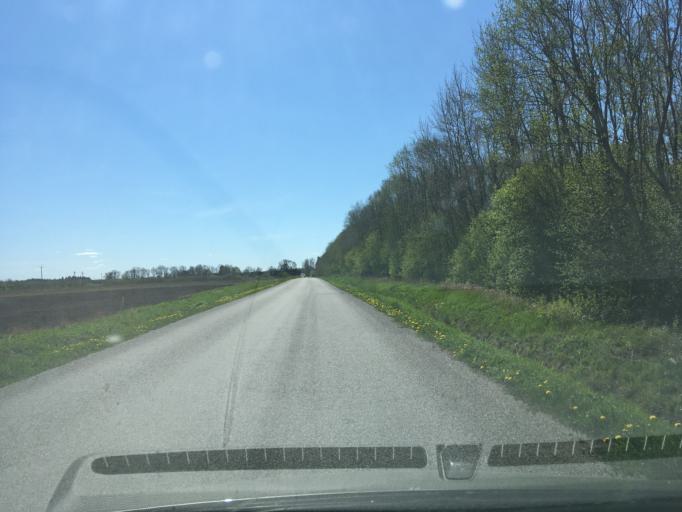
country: EE
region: Harju
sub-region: Raasiku vald
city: Arukula
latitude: 59.3980
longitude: 25.0799
